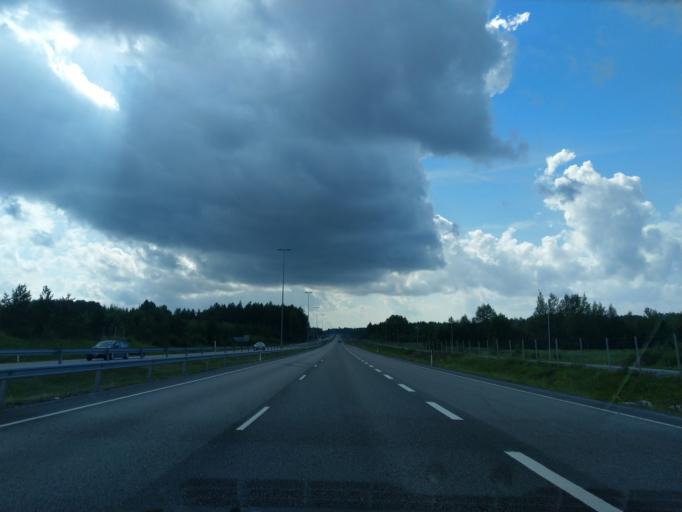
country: FI
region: South Karelia
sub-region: Imatra
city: Imatra
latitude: 61.1829
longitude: 28.7354
